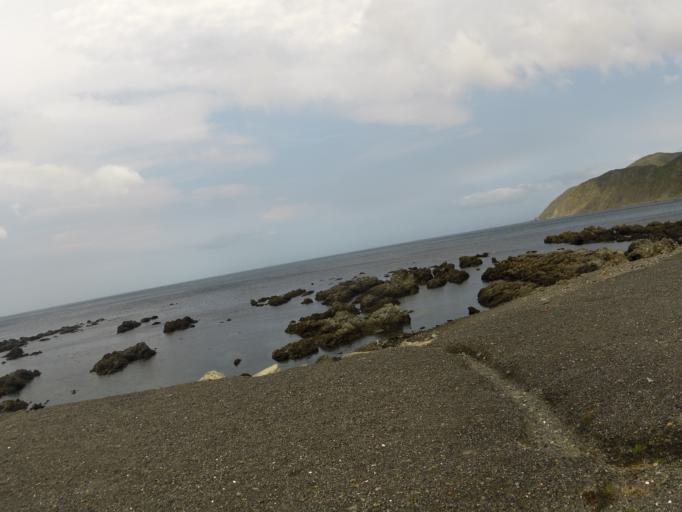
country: NZ
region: Wellington
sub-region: Wellington City
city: Brooklyn
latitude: -41.3487
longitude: 174.7496
